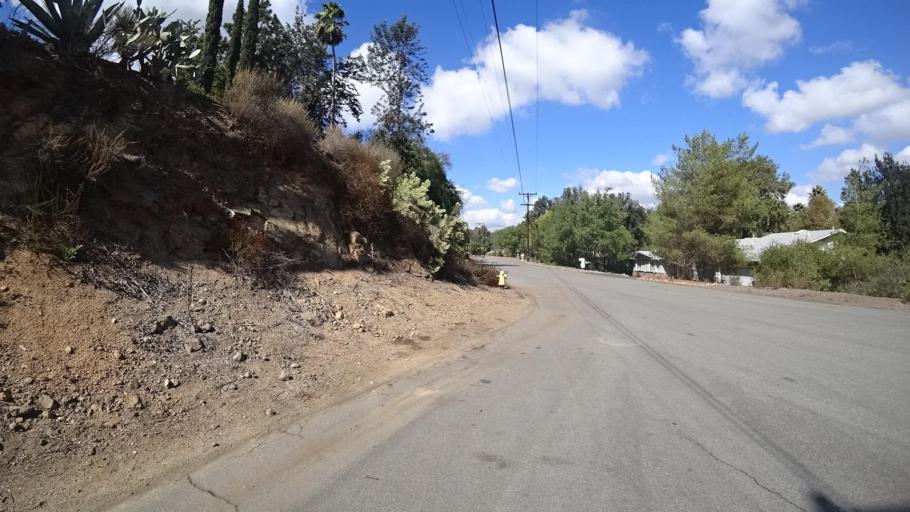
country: US
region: California
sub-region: San Diego County
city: Casa de Oro-Mount Helix
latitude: 32.7592
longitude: -116.9512
